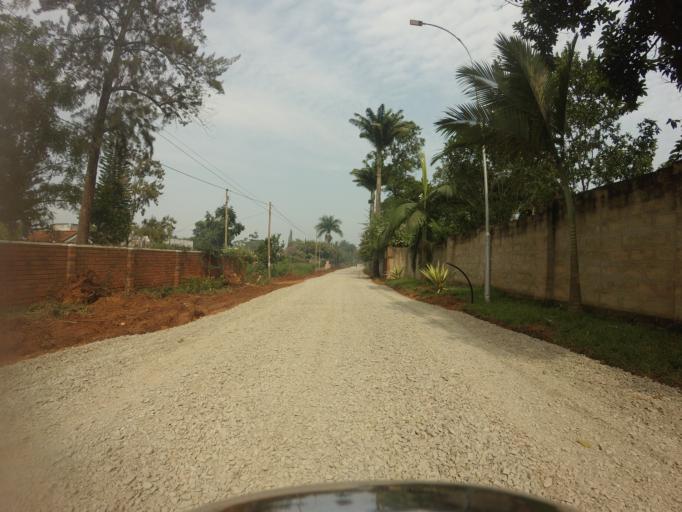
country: UG
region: Central Region
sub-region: Wakiso District
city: Kireka
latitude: 0.2941
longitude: 32.6583
